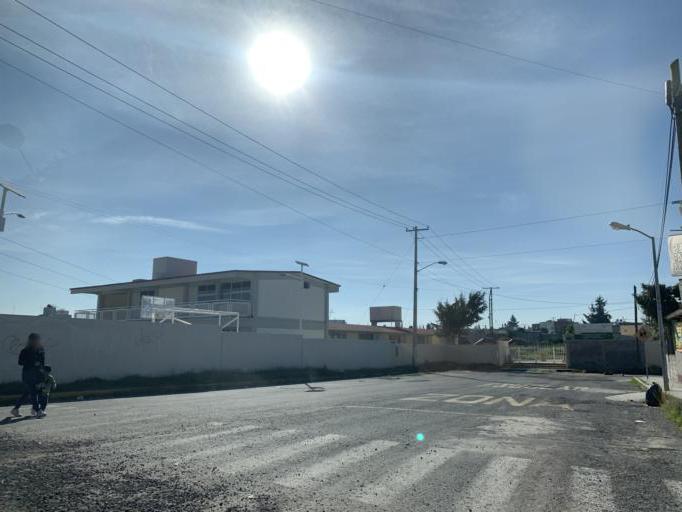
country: MX
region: Puebla
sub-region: Puebla
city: El Capulo (La Quebradora)
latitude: 18.9615
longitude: -98.2457
